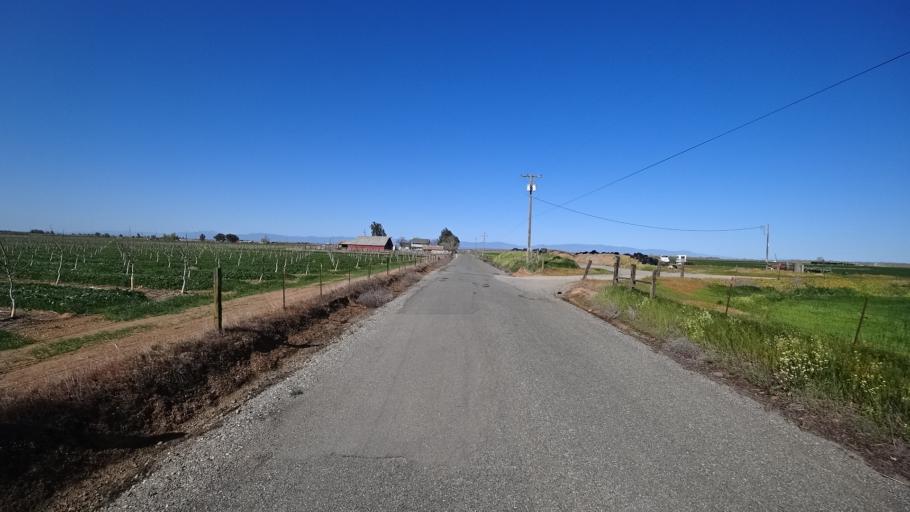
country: US
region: California
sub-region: Glenn County
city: Orland
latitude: 39.7825
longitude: -122.1114
